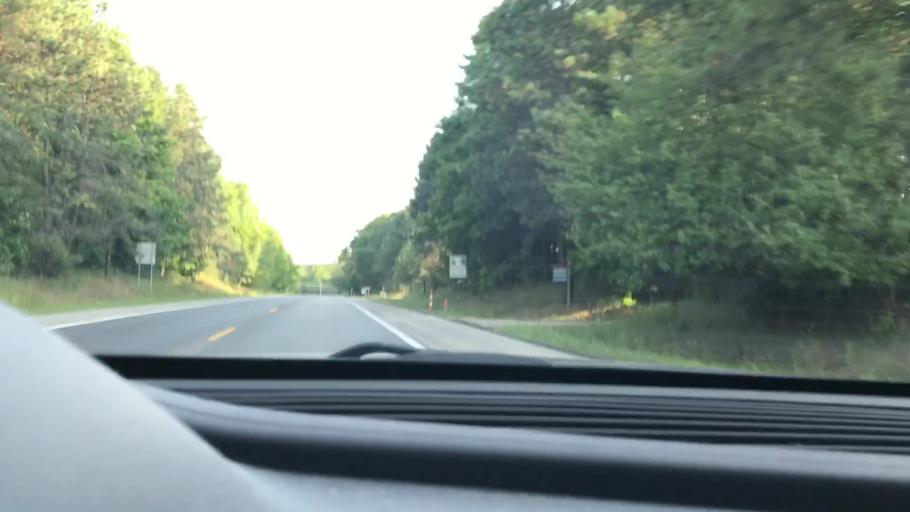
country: US
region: Michigan
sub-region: Antrim County
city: Bellaire
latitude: 45.0495
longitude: -85.3496
